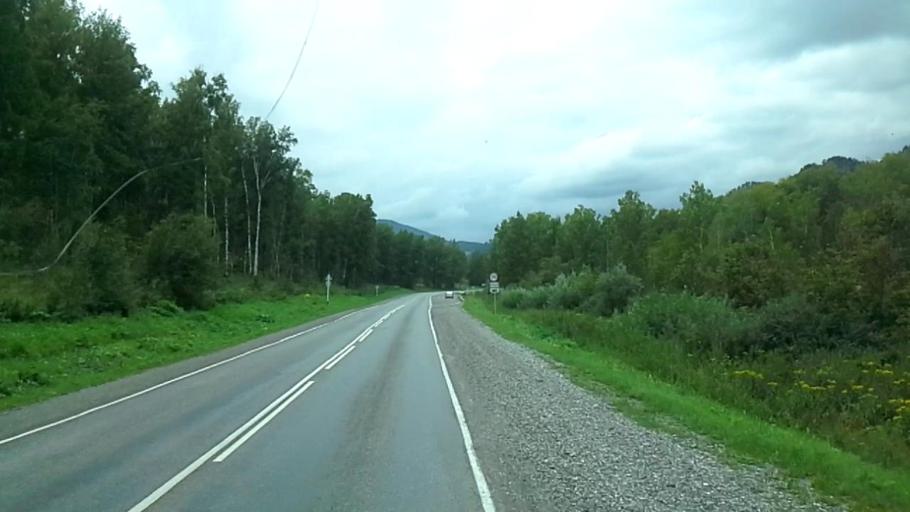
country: RU
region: Altay
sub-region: Mayminskiy Rayon
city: Manzherok
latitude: 51.8580
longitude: 85.7559
